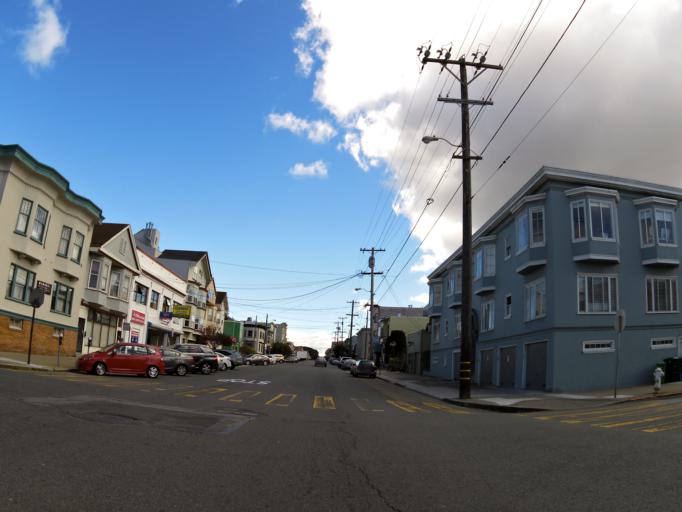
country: US
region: California
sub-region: San Francisco County
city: San Francisco
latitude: 37.7822
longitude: -122.4806
